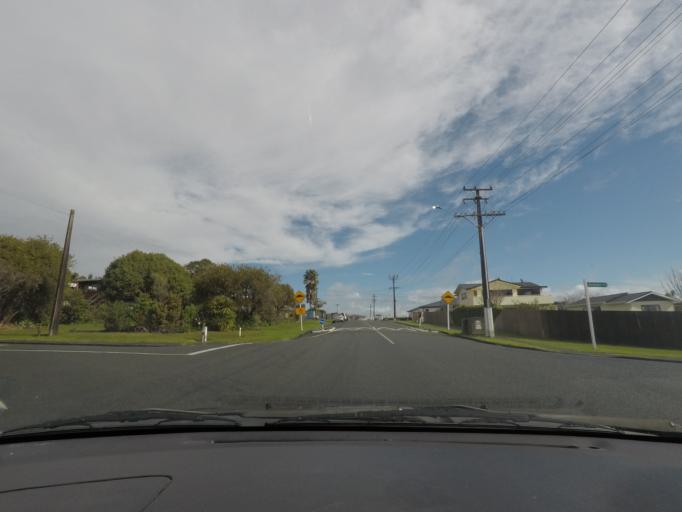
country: NZ
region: Auckland
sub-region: Auckland
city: Warkworth
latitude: -36.4241
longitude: 174.7288
